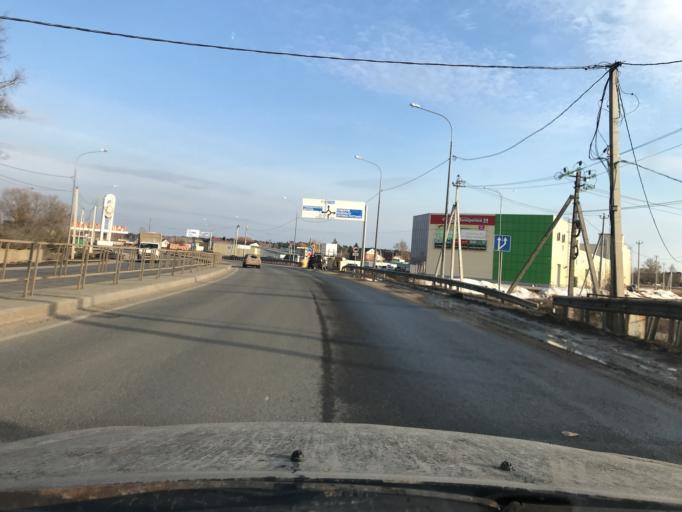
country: RU
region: Kaluga
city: Kaluga
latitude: 54.4700
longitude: 36.2366
